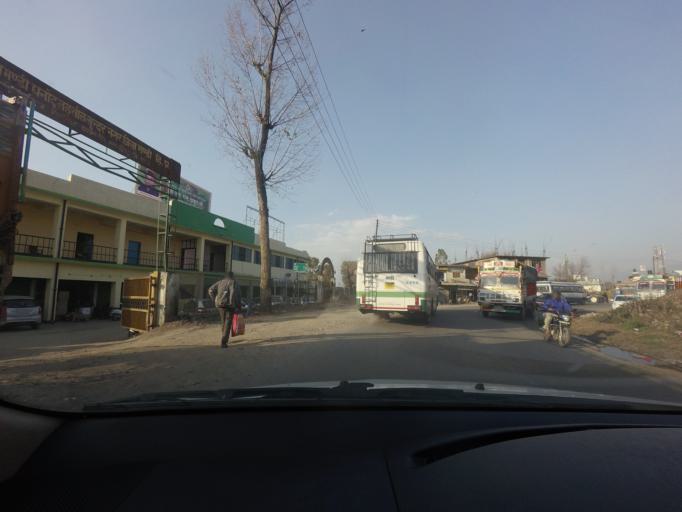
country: IN
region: Himachal Pradesh
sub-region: Mandi
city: Sundarnagar
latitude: 31.5521
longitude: 76.8994
